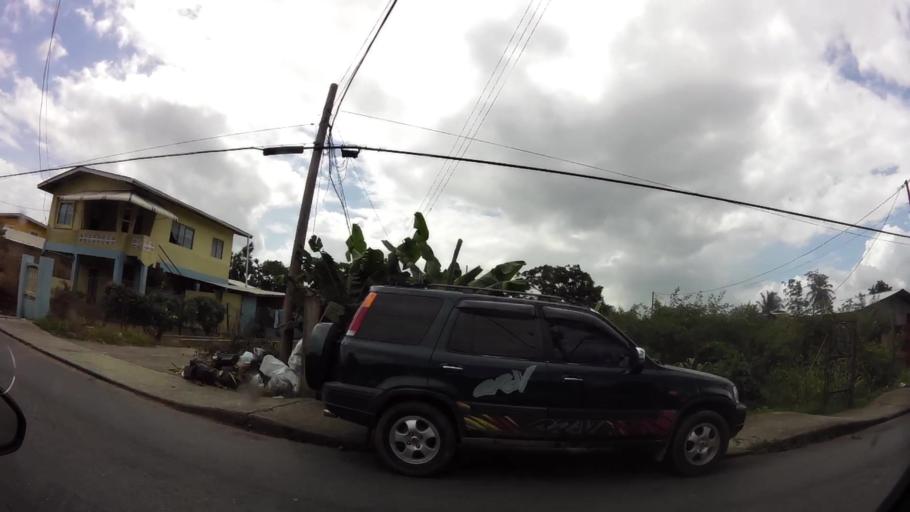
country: TT
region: Tunapuna/Piarco
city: Arouca
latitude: 10.6324
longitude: -61.3253
